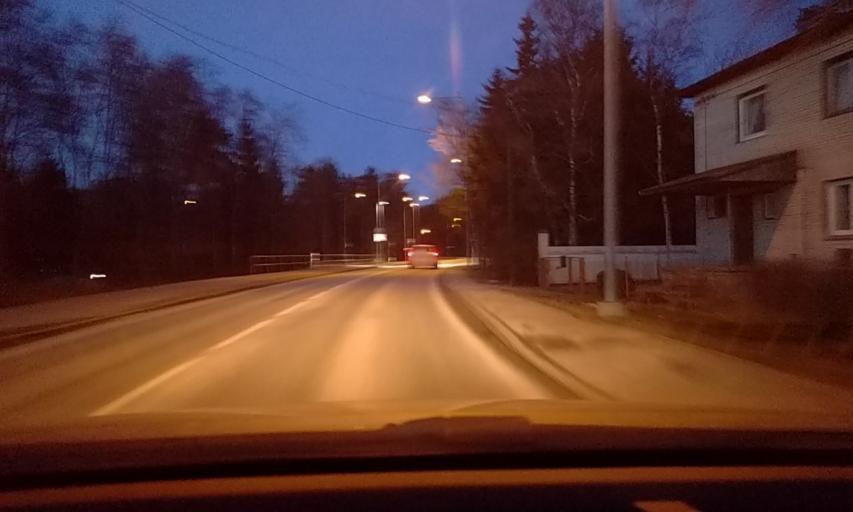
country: EE
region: Harju
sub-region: Viimsi vald
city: Viimsi
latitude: 59.4840
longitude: 24.8605
